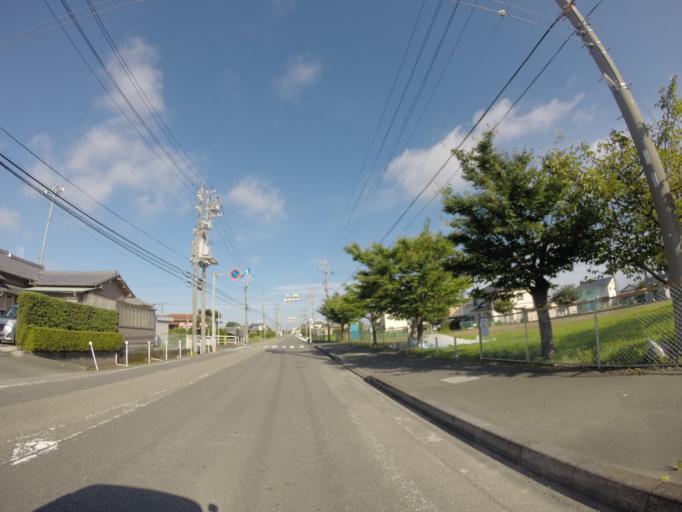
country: JP
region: Shizuoka
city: Yaizu
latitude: 34.8174
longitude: 138.3181
